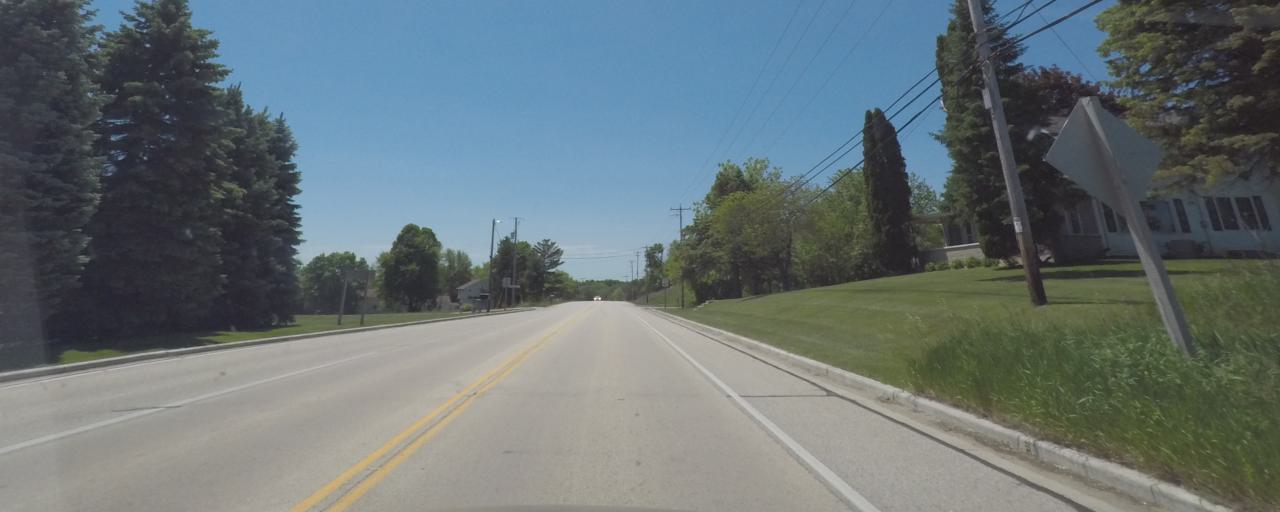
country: US
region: Wisconsin
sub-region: Washington County
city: West Bend
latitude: 43.4543
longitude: -88.1632
